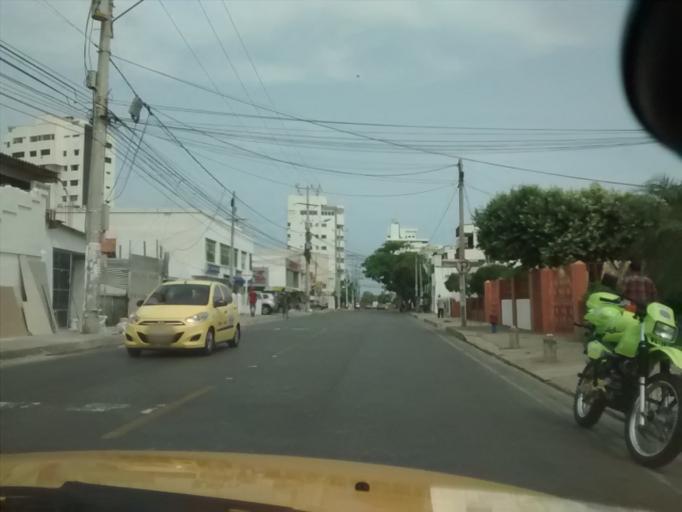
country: CO
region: Bolivar
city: Cartagena
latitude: 10.4160
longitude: -75.5398
